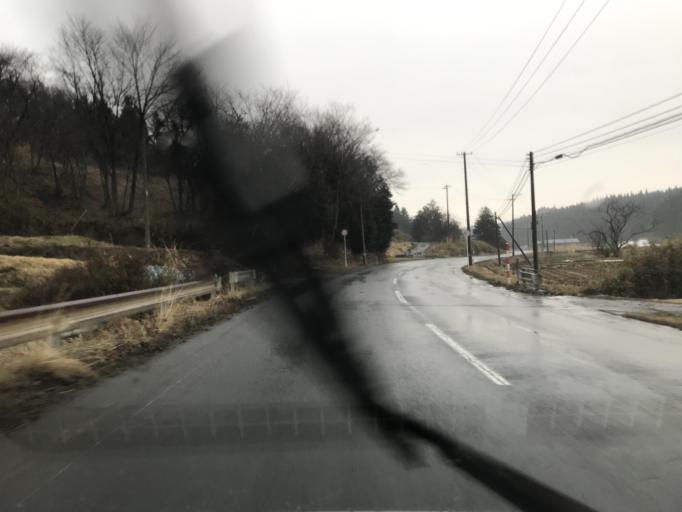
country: JP
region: Miyagi
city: Furukawa
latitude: 38.6944
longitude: 140.9234
